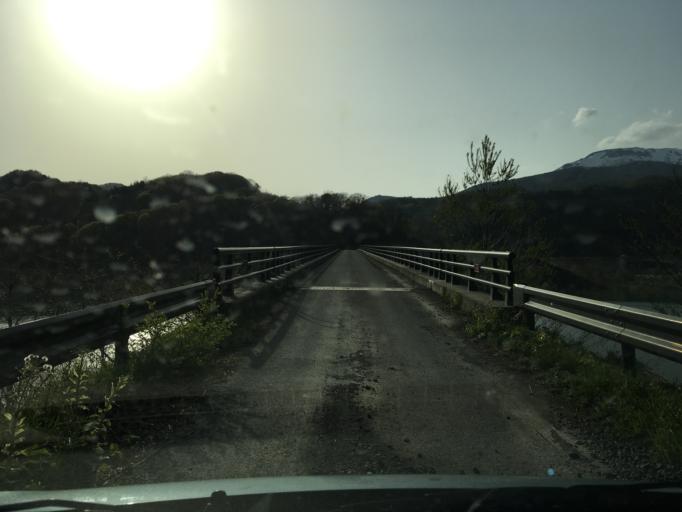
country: JP
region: Iwate
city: Mizusawa
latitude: 39.1005
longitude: 140.8852
